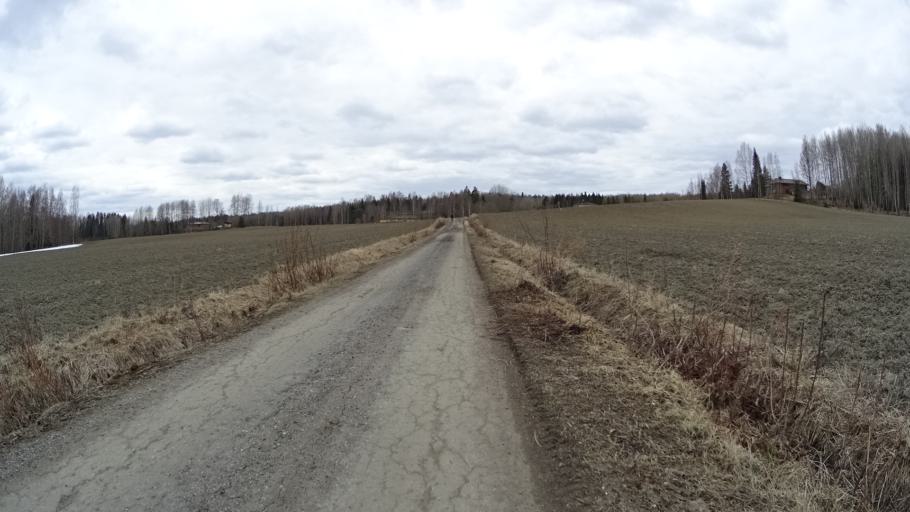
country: FI
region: Uusimaa
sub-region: Helsinki
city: Kilo
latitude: 60.2958
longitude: 24.7927
